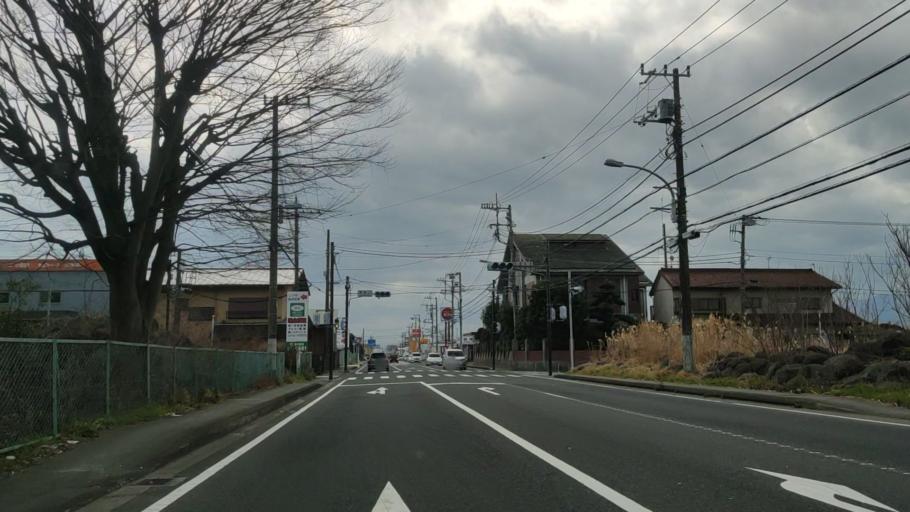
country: JP
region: Kanagawa
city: Odawara
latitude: 35.3014
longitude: 139.1667
